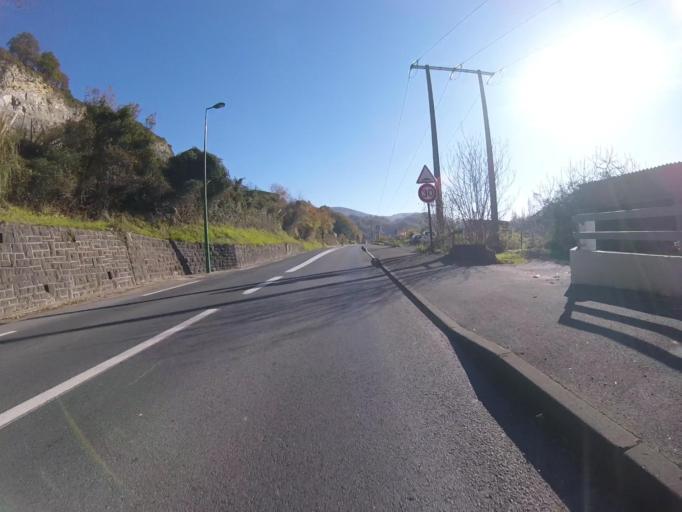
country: FR
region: Aquitaine
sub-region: Departement des Pyrenees-Atlantiques
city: Hendaye
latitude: 43.3439
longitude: -1.7565
